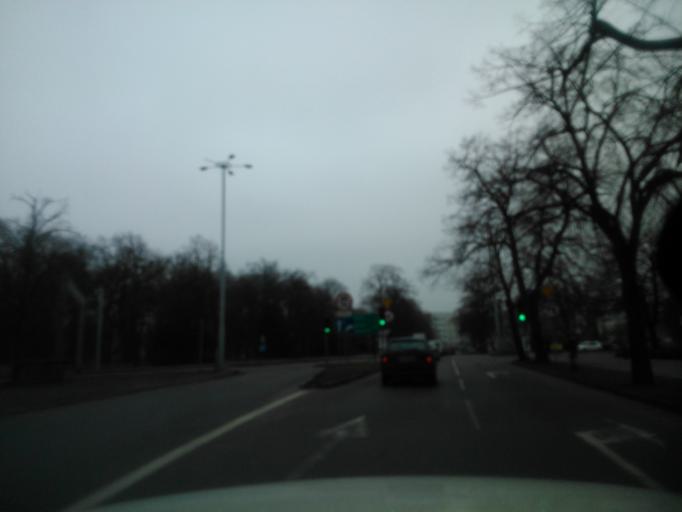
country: PL
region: Kujawsko-Pomorskie
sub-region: Torun
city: Torun
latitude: 53.0115
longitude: 18.5996
